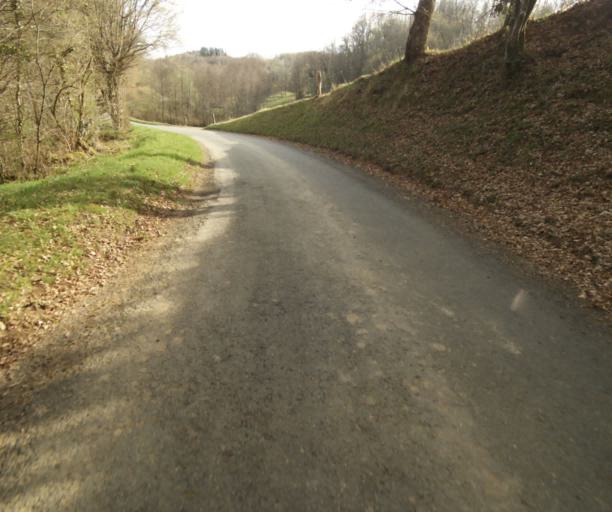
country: FR
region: Limousin
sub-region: Departement de la Correze
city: Naves
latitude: 45.2996
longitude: 1.7547
